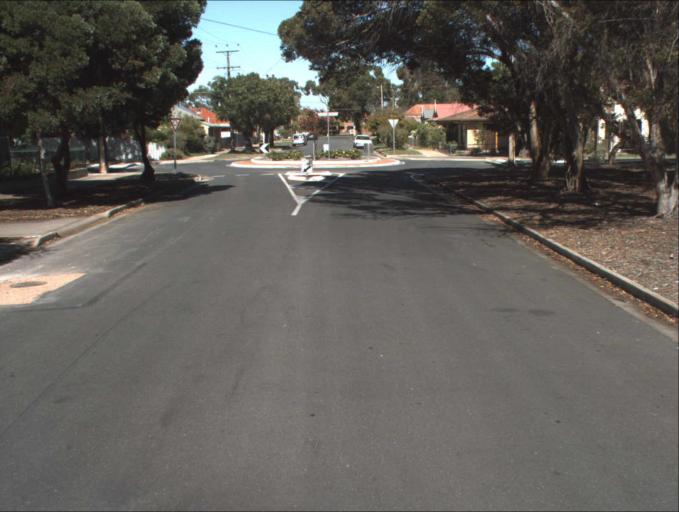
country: AU
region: South Australia
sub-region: Port Adelaide Enfield
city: Alberton
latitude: -34.8582
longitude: 138.5149
